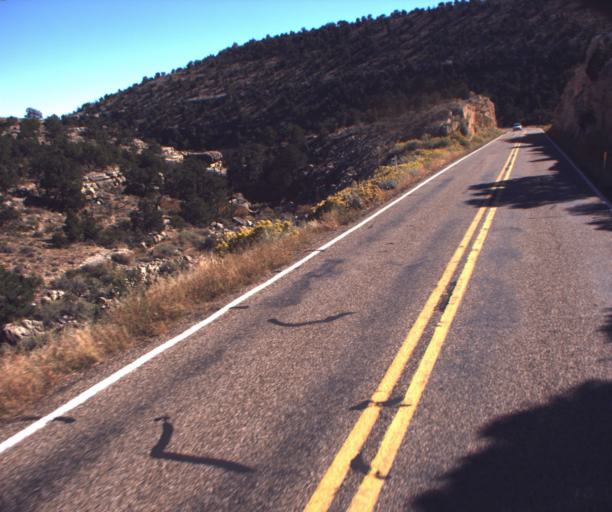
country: US
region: Arizona
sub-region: Coconino County
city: Fredonia
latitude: 36.7279
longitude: -112.0865
